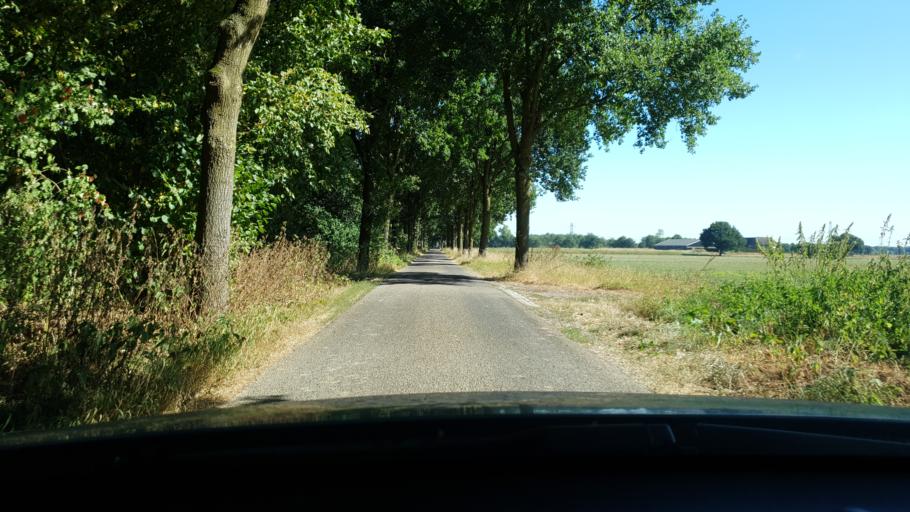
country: NL
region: North Brabant
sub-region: Gemeente Grave
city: Grave
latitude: 51.7699
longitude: 5.7686
